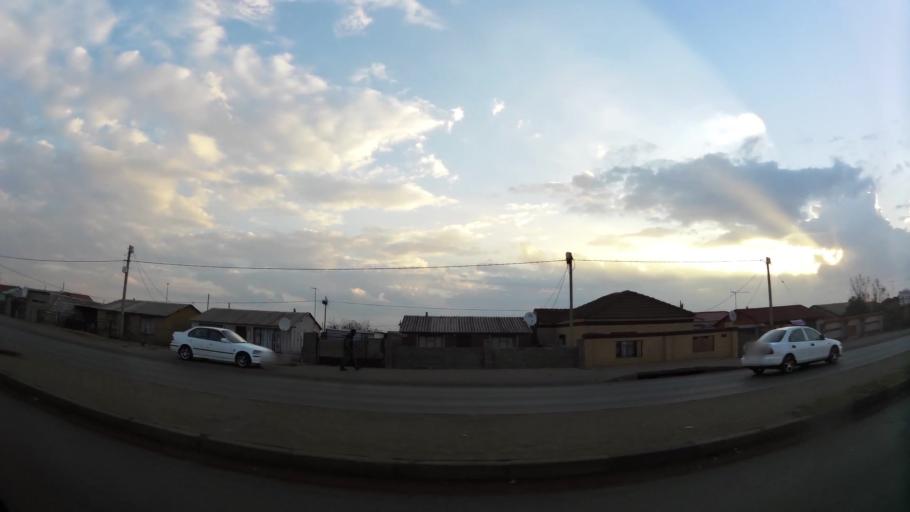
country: ZA
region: Gauteng
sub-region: City of Johannesburg Metropolitan Municipality
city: Orange Farm
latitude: -26.5717
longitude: 27.8380
